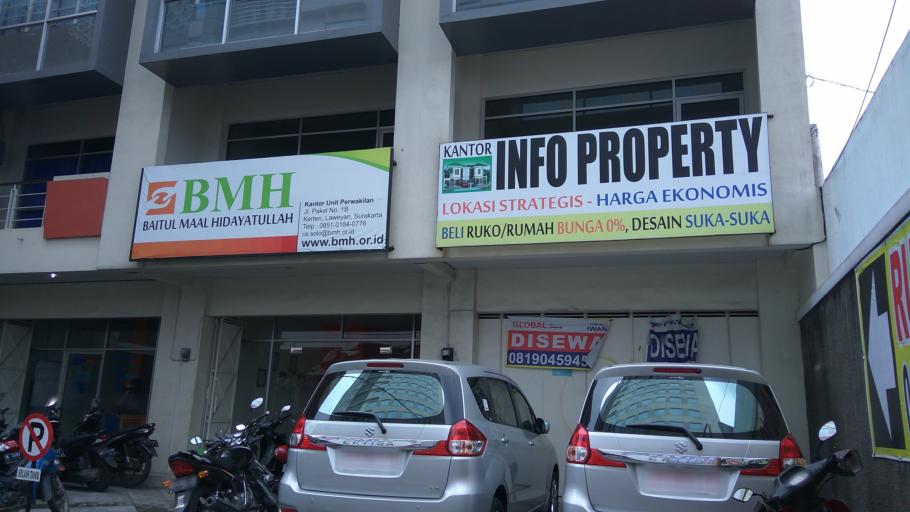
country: ID
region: Central Java
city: Surakarta
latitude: -7.5519
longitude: 110.7952
